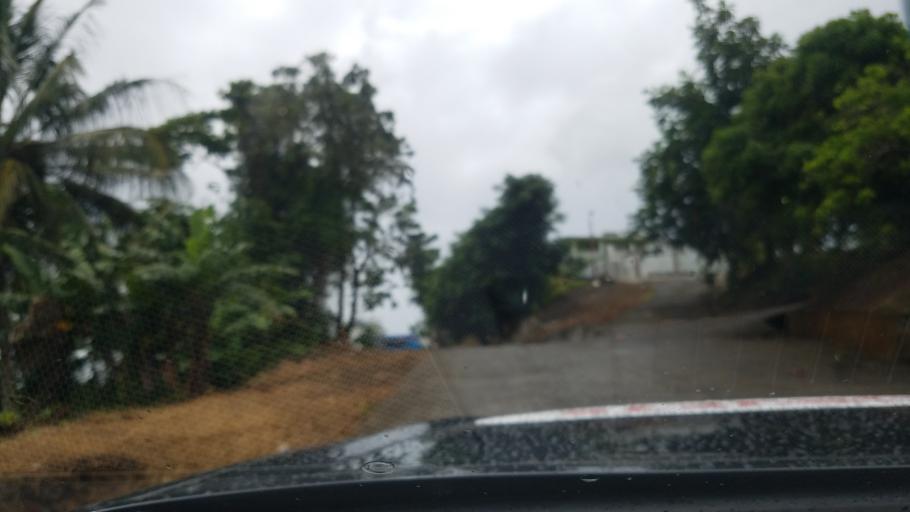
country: LC
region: Castries Quarter
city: Bisee
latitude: 13.9984
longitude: -60.9578
